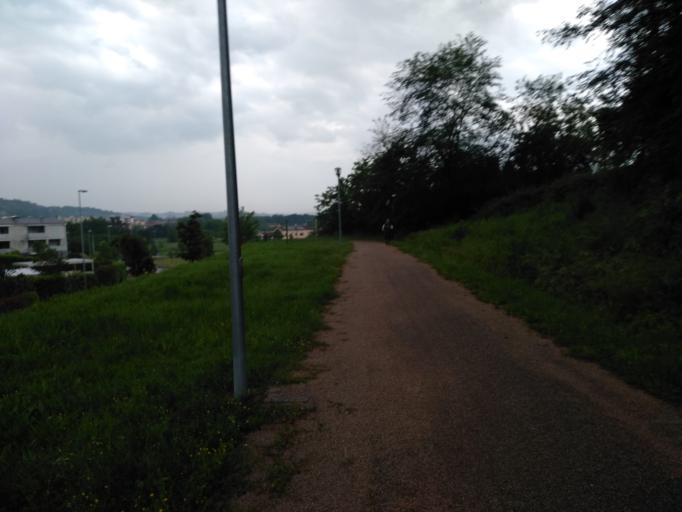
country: IT
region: Tuscany
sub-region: Province of Arezzo
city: San Giovanni Valdarno
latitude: 43.5580
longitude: 11.5282
